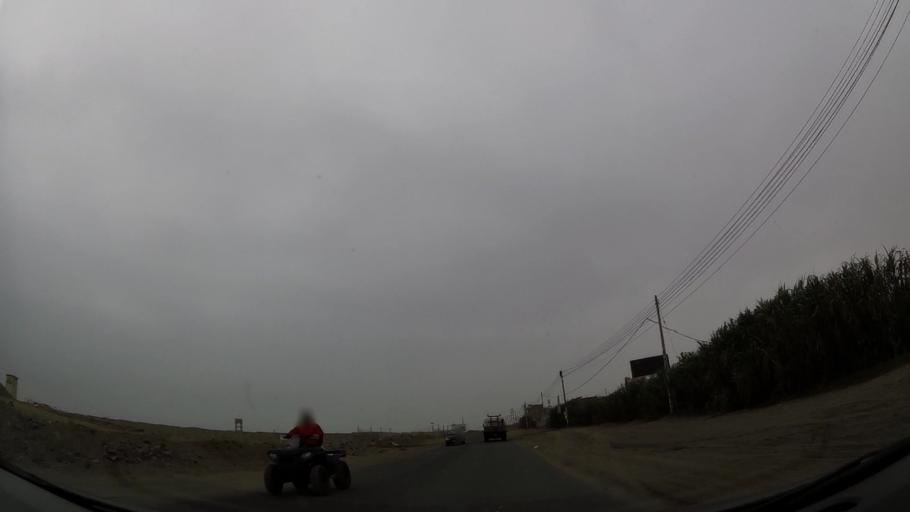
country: PE
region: Lima
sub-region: Lima
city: Punta Hermosa
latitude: -12.3267
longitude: -76.8253
